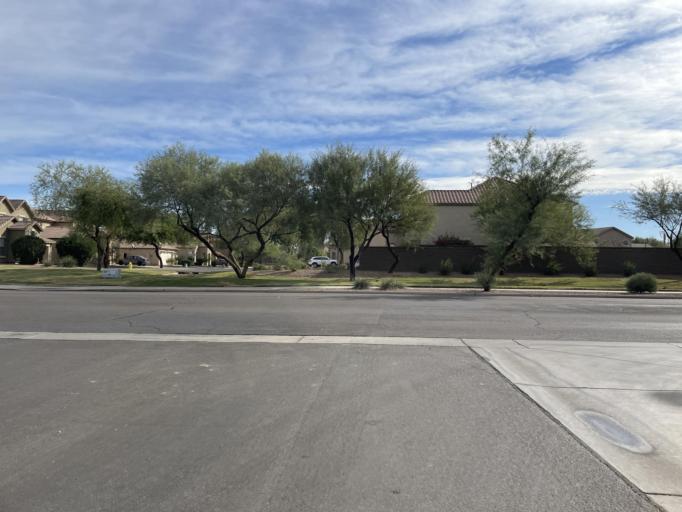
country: US
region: Arizona
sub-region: Maricopa County
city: Queen Creek
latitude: 33.2723
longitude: -111.7075
